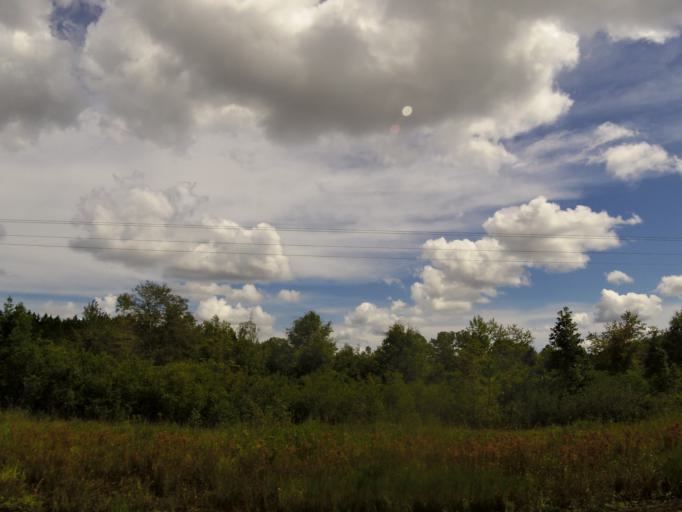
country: US
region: Georgia
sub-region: Brantley County
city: Nahunta
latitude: 31.1463
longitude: -81.9919
